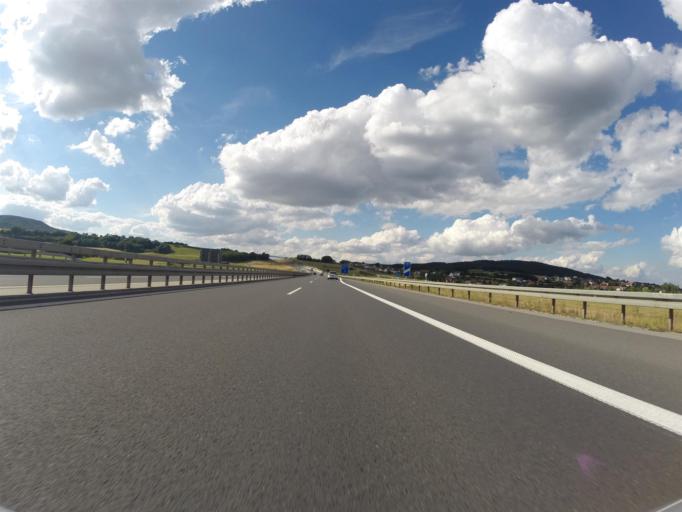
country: DE
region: Bavaria
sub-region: Upper Franconia
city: Lichtenfels
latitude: 50.1419
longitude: 11.0339
